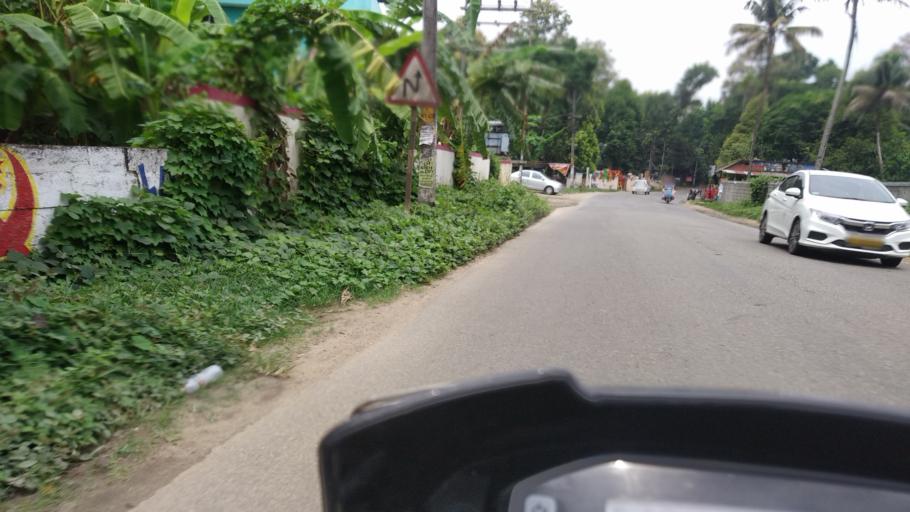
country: IN
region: Kerala
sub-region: Ernakulam
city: Perumpavur
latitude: 10.1090
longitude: 76.5356
